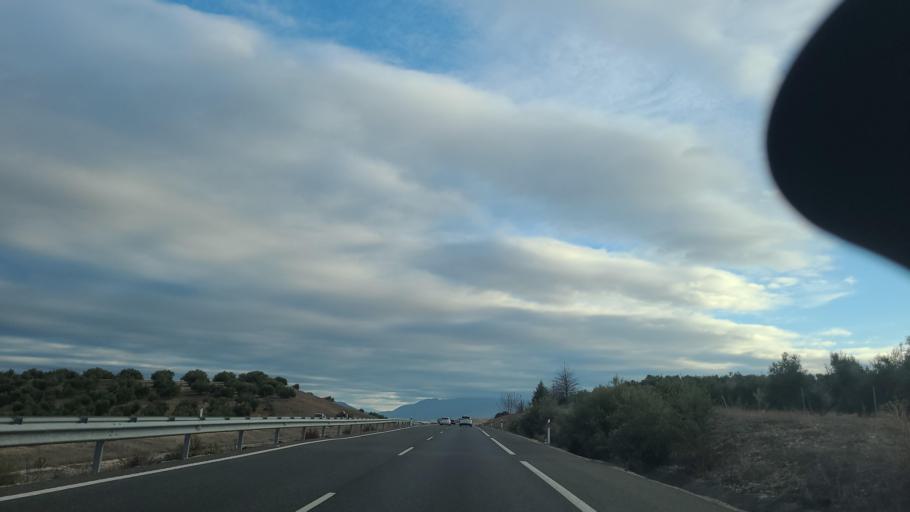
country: ES
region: Andalusia
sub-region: Provincia de Jaen
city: Mengibar
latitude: 37.8740
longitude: -3.7676
